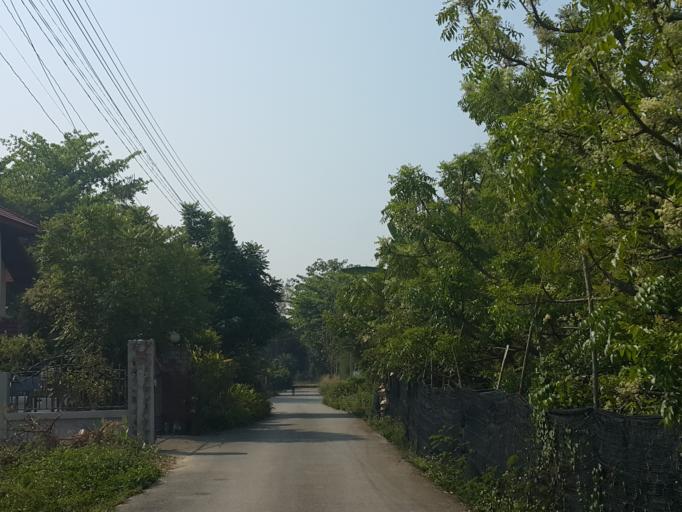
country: TH
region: Chiang Mai
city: Saraphi
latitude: 18.7255
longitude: 99.0200
